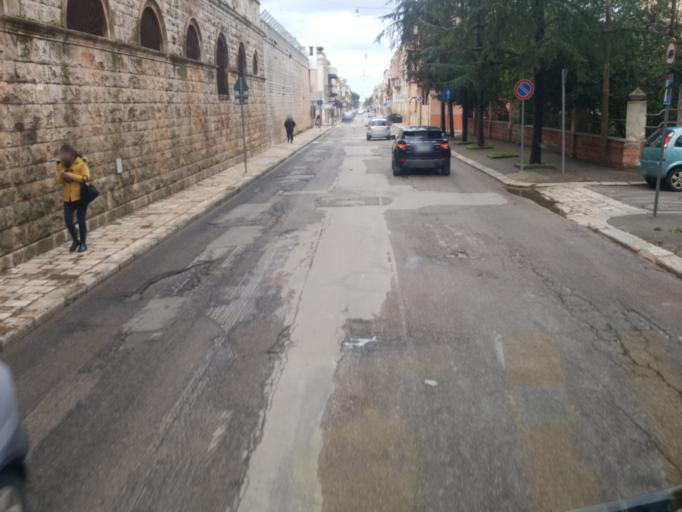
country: IT
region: Apulia
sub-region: Provincia di Bari
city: Turi
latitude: 40.9173
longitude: 17.0195
